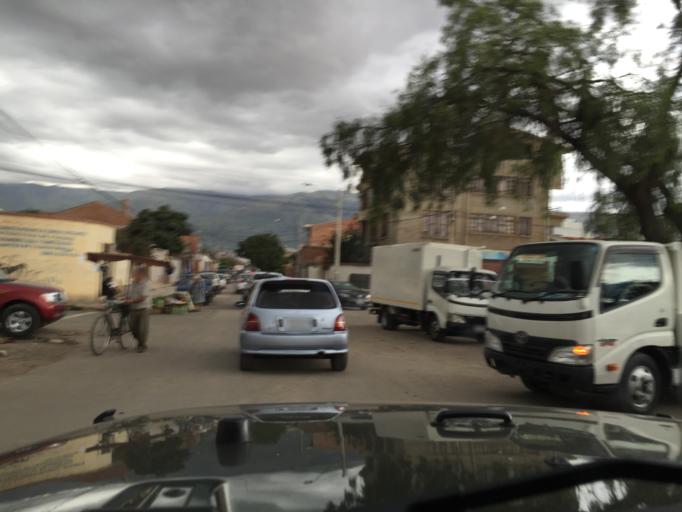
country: BO
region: Cochabamba
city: Cochabamba
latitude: -17.4004
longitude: -66.1878
